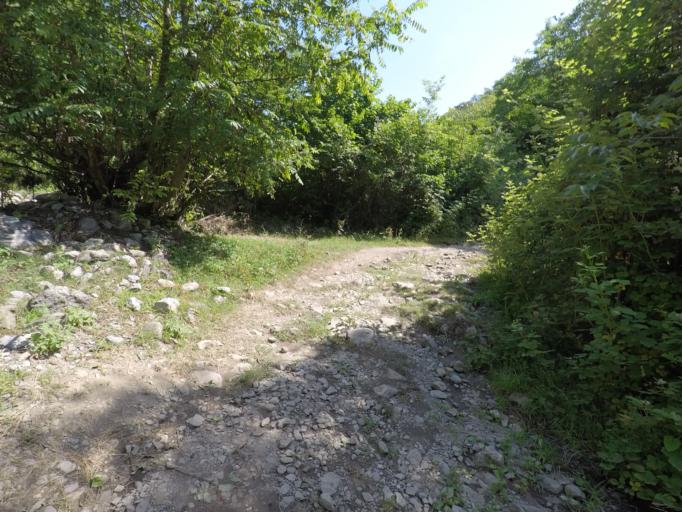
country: AZ
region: Qakh Rayon
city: Cinarli
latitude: 41.4899
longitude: 46.8571
